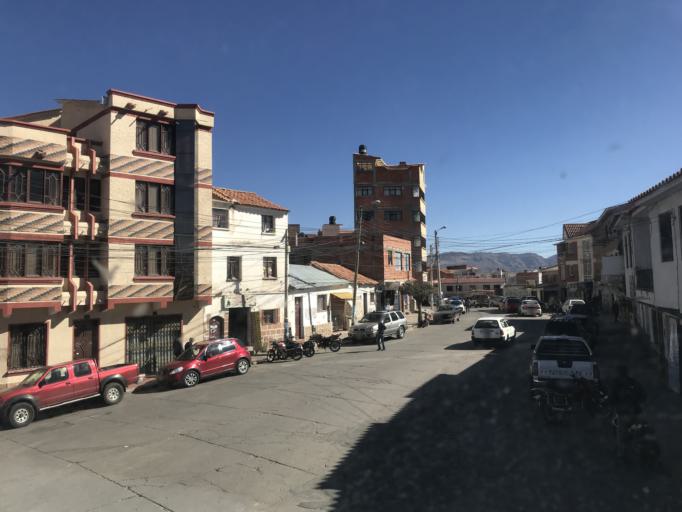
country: BO
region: Chuquisaca
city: Sucre
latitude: -19.0426
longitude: -65.2479
